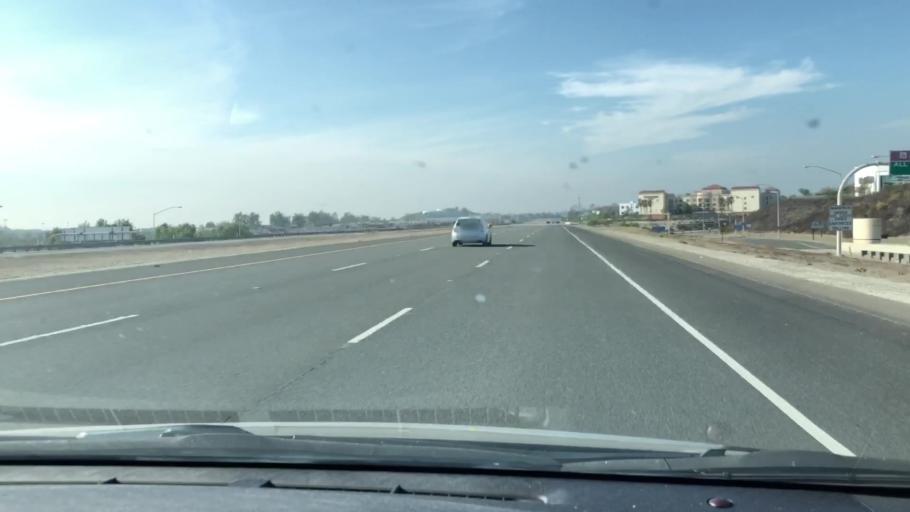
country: US
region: California
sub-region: Orange County
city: Portola Hills
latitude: 33.6667
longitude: -117.6474
